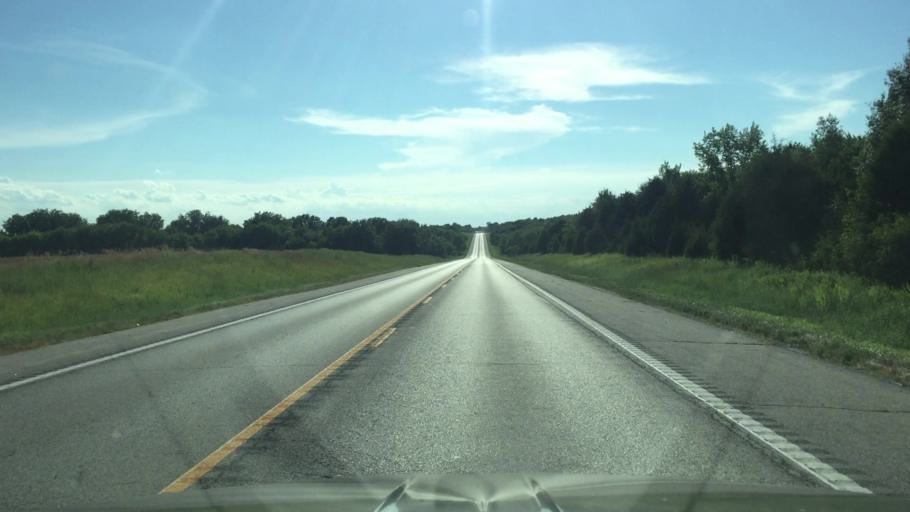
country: US
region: Missouri
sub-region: Pettis County
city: Sedalia
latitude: 38.6943
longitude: -93.1124
